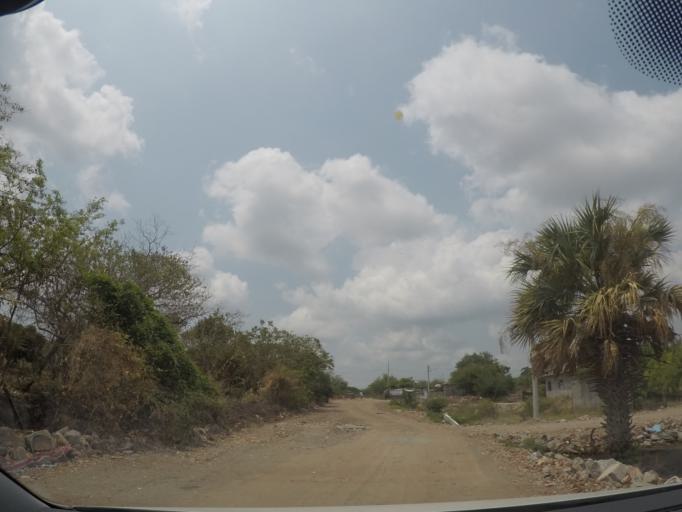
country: MX
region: Oaxaca
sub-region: El Espinal
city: El Espinal
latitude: 16.4759
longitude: -95.0424
